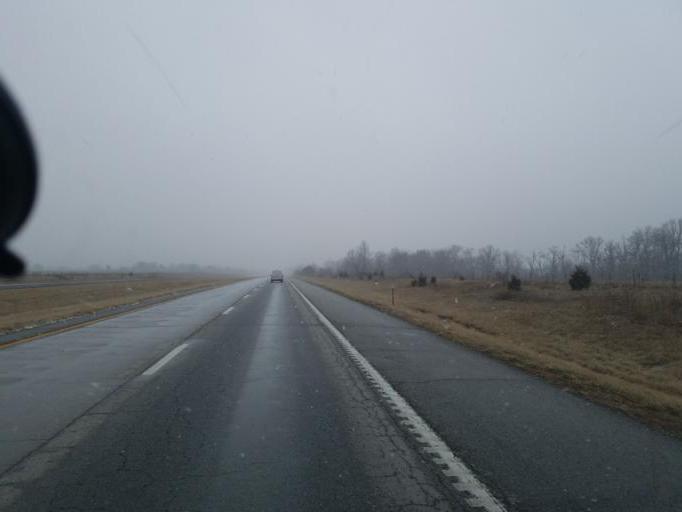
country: US
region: Missouri
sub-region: Macon County
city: La Plata
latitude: 39.9794
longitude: -92.4761
